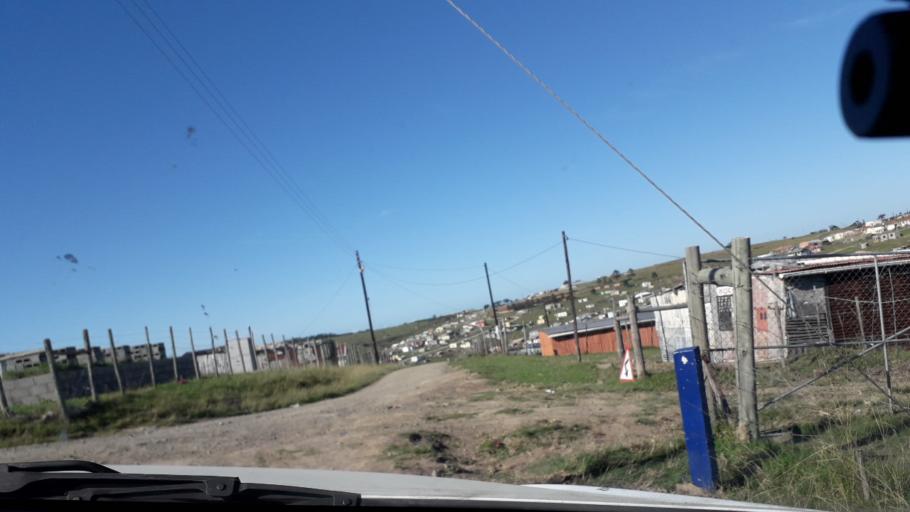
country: ZA
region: Eastern Cape
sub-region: Buffalo City Metropolitan Municipality
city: East London
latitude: -32.8456
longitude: 27.9852
